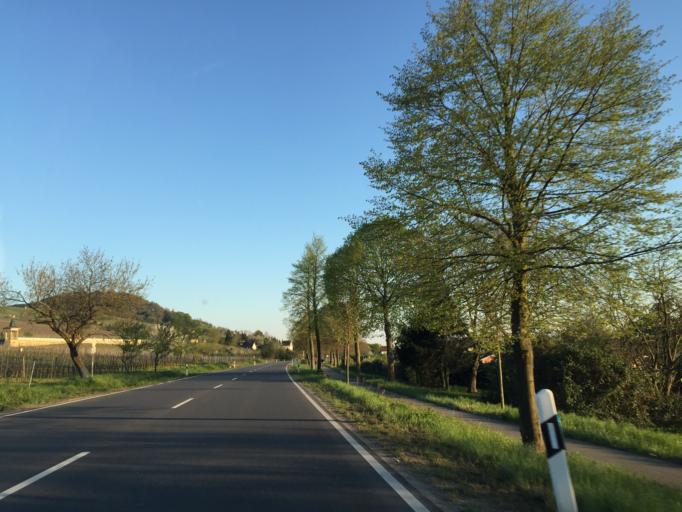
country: DE
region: Hesse
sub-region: Regierungsbezirk Darmstadt
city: Heppenheim an der Bergstrasse
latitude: 49.6602
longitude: 8.6347
